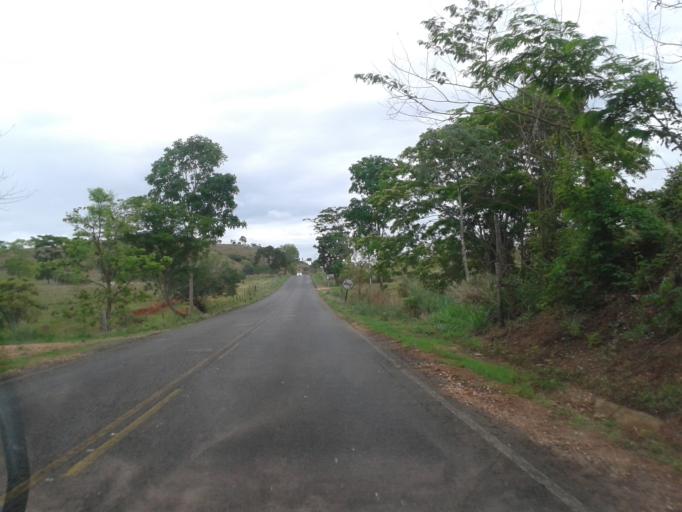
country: BR
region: Goias
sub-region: Caldas Novas
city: Caldas Novas
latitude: -18.0618
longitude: -48.6944
